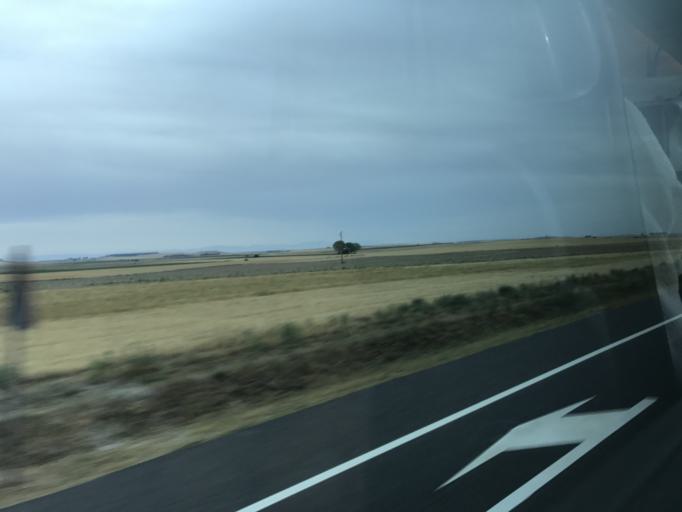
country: ES
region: Castille and Leon
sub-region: Provincia de Segovia
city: Rapariegos
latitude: 41.0881
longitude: -4.6371
